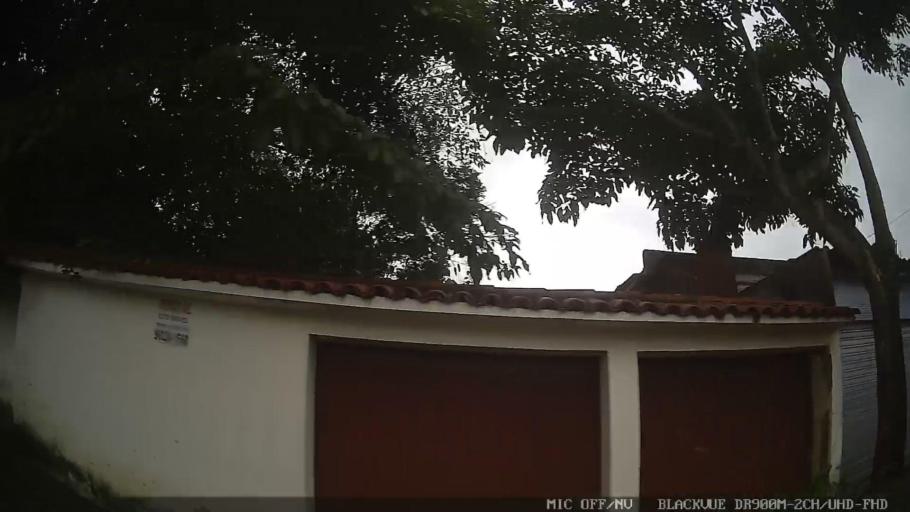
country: BR
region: Sao Paulo
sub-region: Mogi das Cruzes
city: Mogi das Cruzes
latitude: -23.5223
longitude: -46.1652
